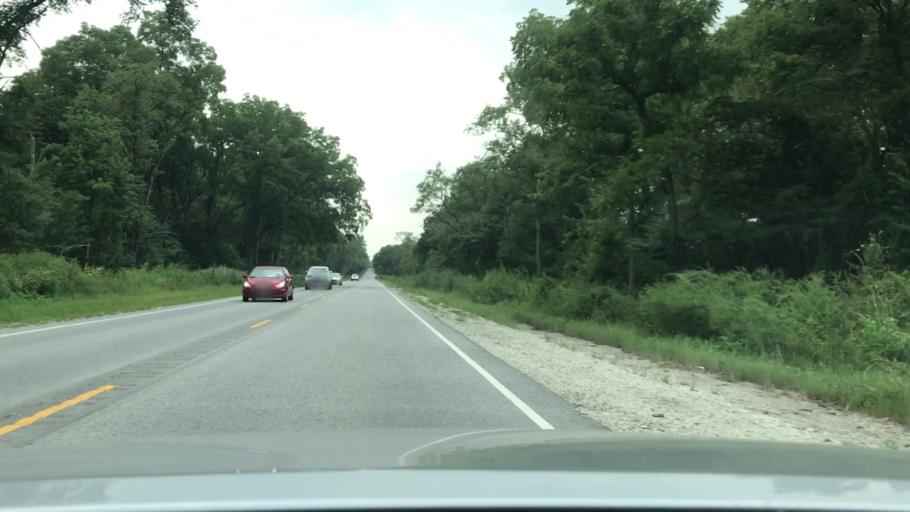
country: US
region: Illinois
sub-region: DuPage County
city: Burr Ridge
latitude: 41.6878
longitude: -87.9034
